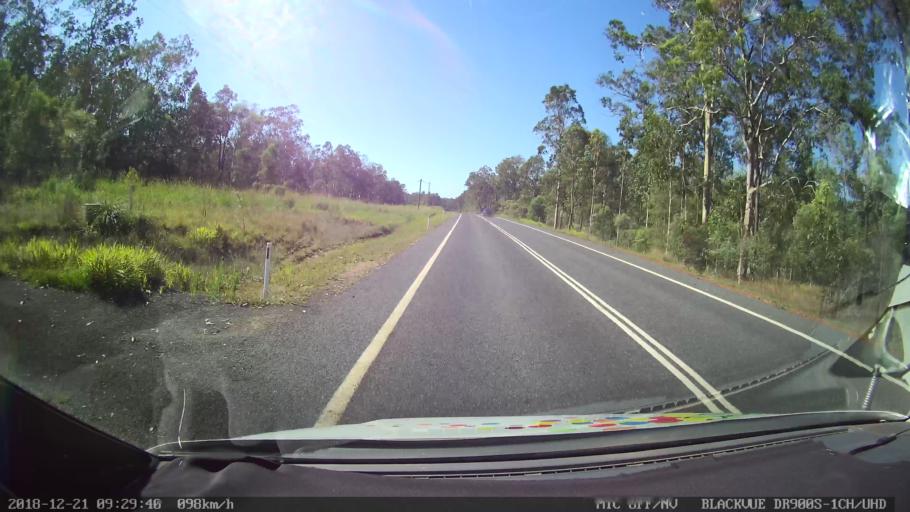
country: AU
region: New South Wales
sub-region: Clarence Valley
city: Maclean
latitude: -29.4352
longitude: 152.9900
